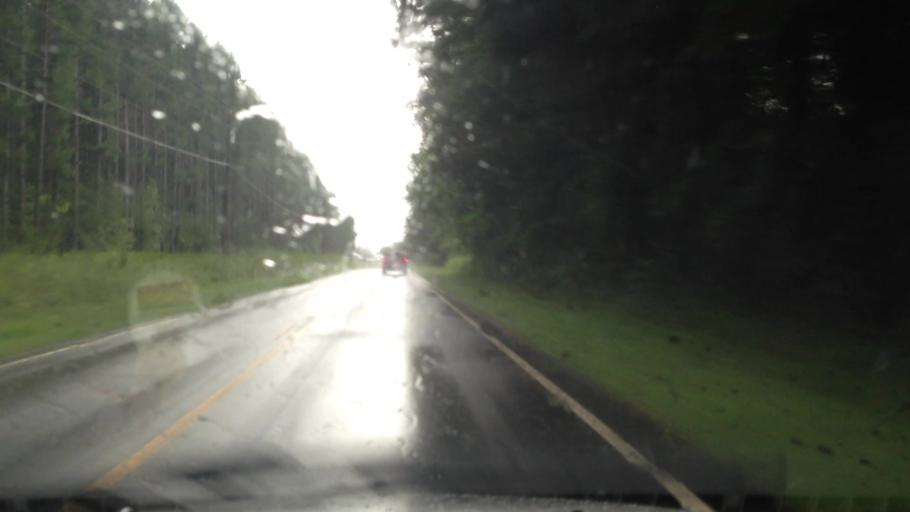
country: US
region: North Carolina
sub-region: Rockingham County
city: Reidsville
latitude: 36.2772
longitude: -79.7365
